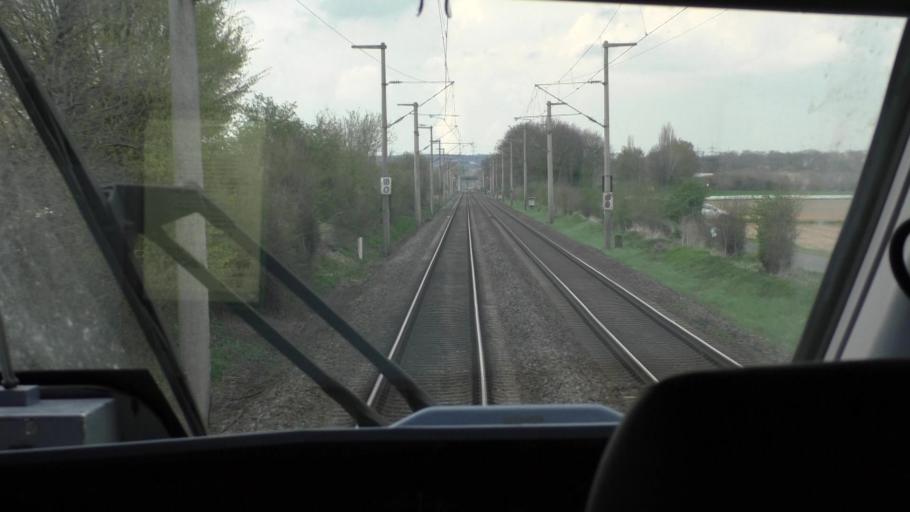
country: DE
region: North Rhine-Westphalia
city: Wesseling
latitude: 50.8046
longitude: 6.9447
